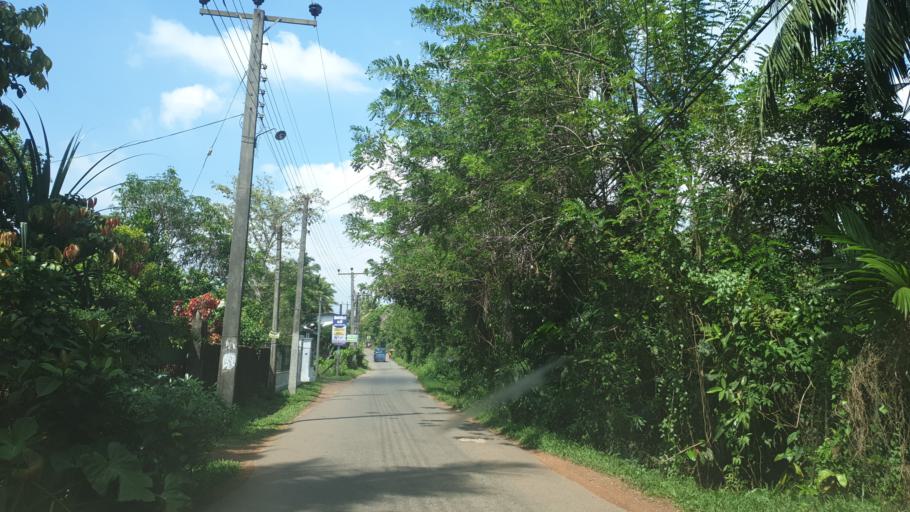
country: LK
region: Western
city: Horana South
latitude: 6.7065
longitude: 79.9840
